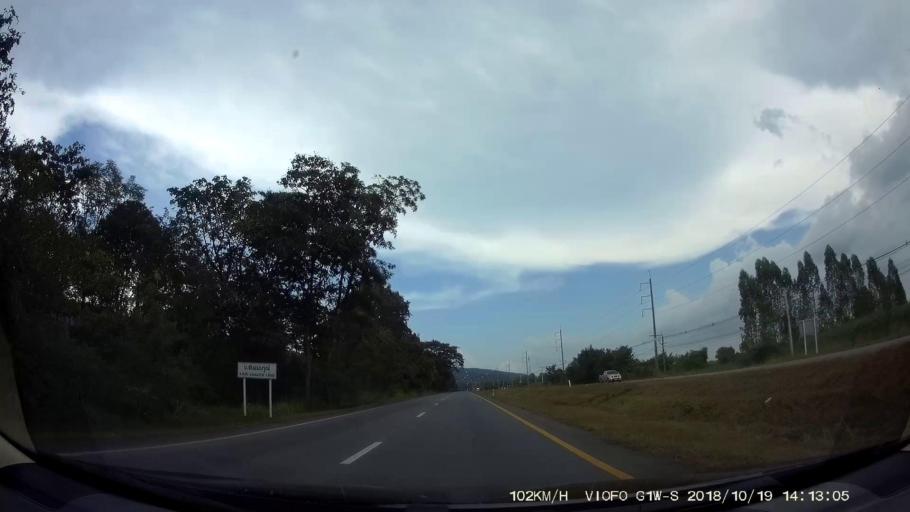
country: TH
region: Chaiyaphum
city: Khon Sawan
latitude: 15.9565
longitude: 102.1784
